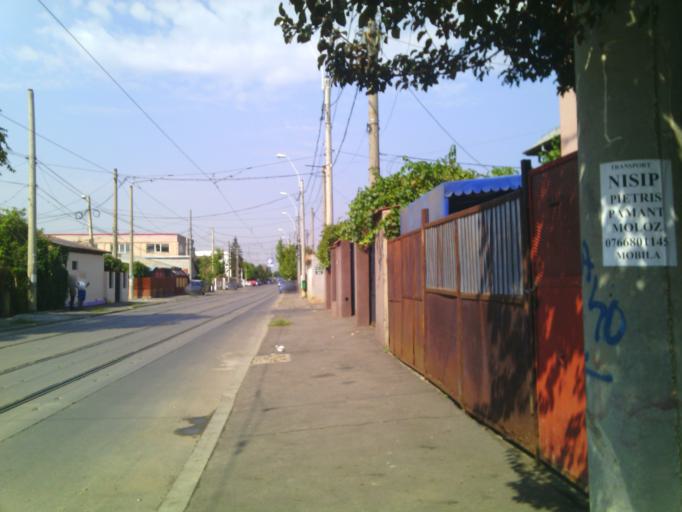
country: RO
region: Ilfov
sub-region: Comuna Jilava
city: Jilava
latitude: 44.3708
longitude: 26.0977
